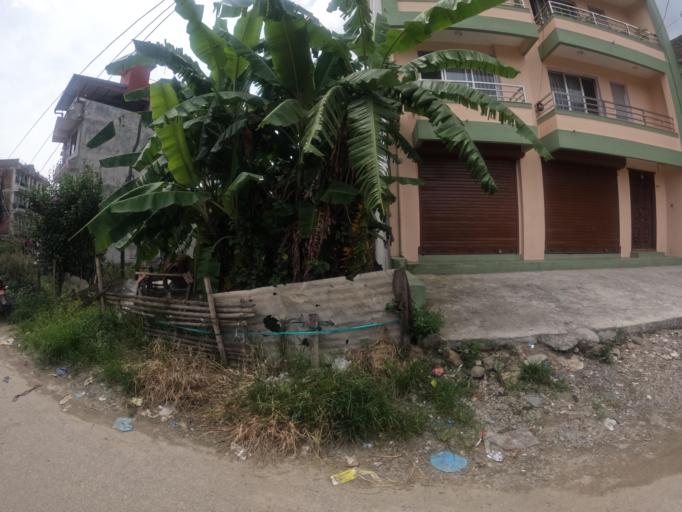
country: NP
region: Central Region
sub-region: Bagmati Zone
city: Bhaktapur
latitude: 27.6887
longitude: 85.3862
